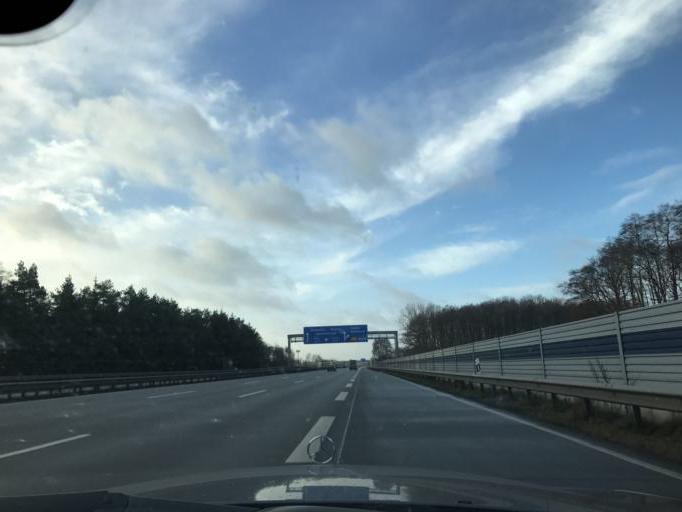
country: DE
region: Lower Saxony
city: Gyhum
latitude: 53.2000
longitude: 9.2945
